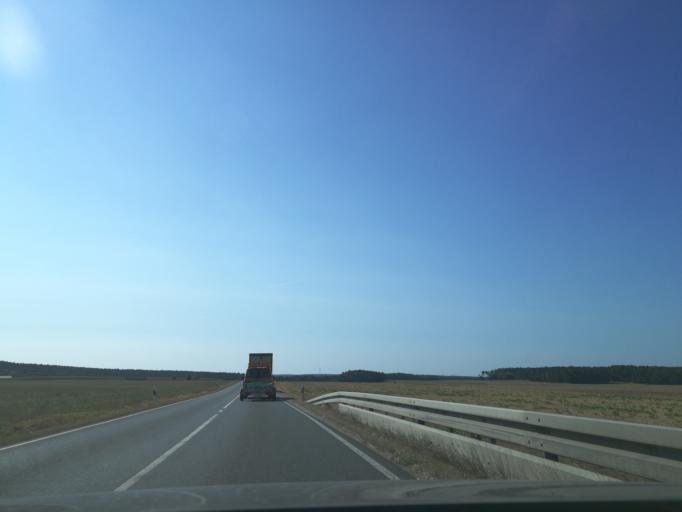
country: DE
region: Bavaria
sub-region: Regierungsbezirk Mittelfranken
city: Cadolzburg
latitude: 49.4466
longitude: 10.8473
